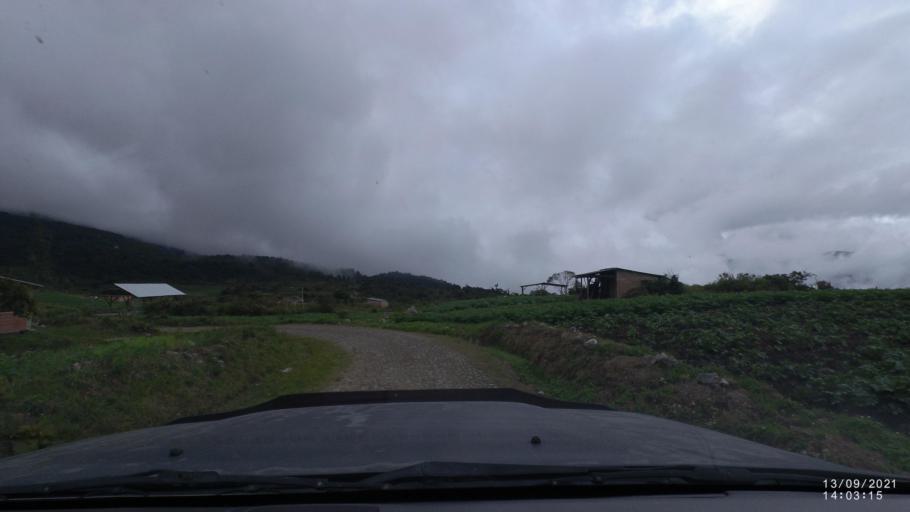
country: BO
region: Cochabamba
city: Colomi
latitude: -17.2055
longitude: -65.8665
